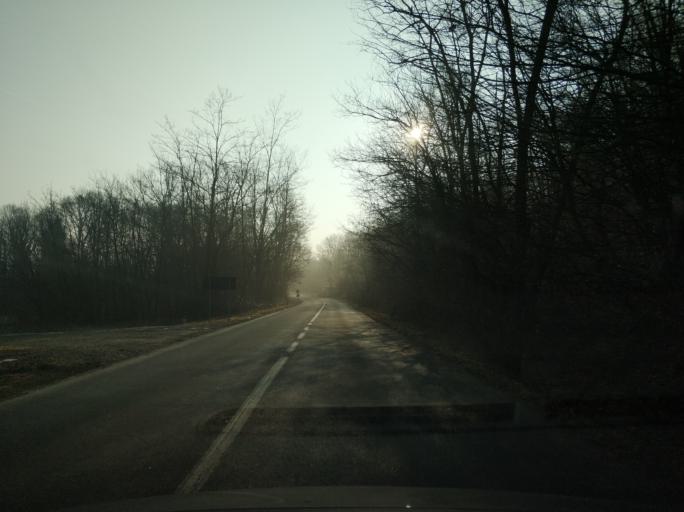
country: IT
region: Piedmont
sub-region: Provincia di Torino
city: Rivarossa
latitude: 45.2562
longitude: 7.7055
